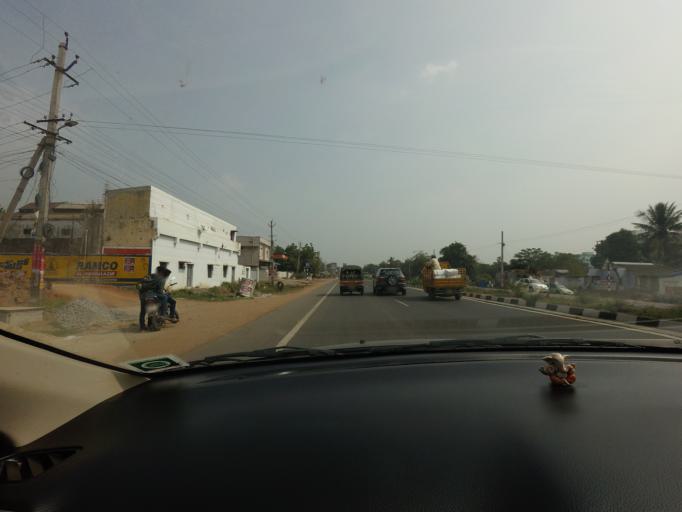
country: IN
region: Andhra Pradesh
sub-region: Krishna
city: Yanamalakuduru
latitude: 16.4818
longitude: 80.6922
